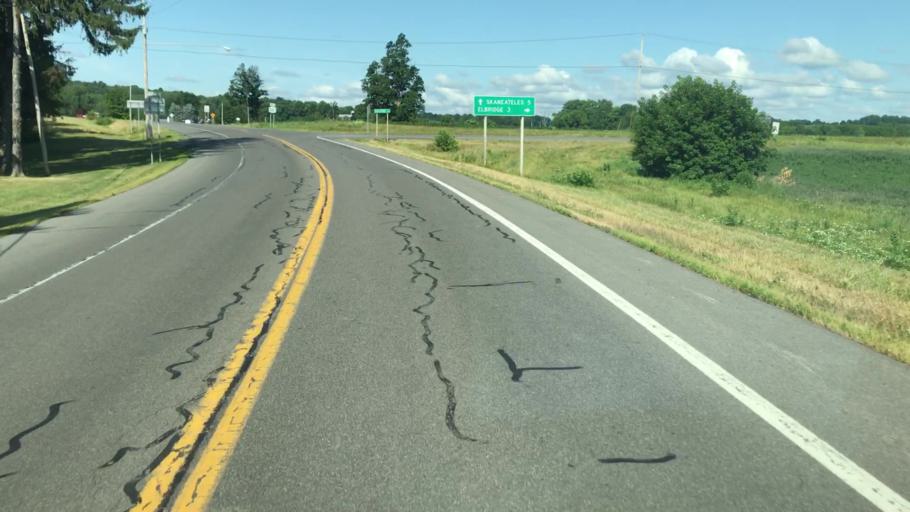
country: US
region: New York
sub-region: Onondaga County
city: Elbridge
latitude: 43.0180
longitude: -76.3899
